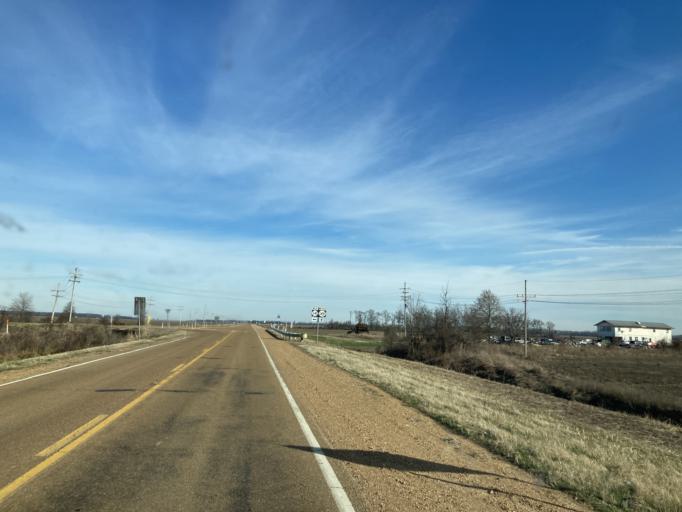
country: US
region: Mississippi
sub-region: Humphreys County
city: Belzoni
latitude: 32.9947
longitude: -90.5883
